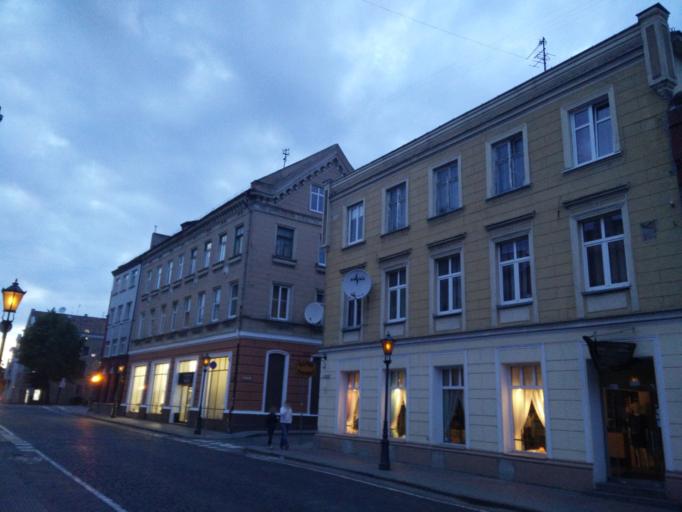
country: LT
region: Klaipedos apskritis
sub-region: Klaipeda
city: Klaipeda
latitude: 55.7085
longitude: 21.1359
